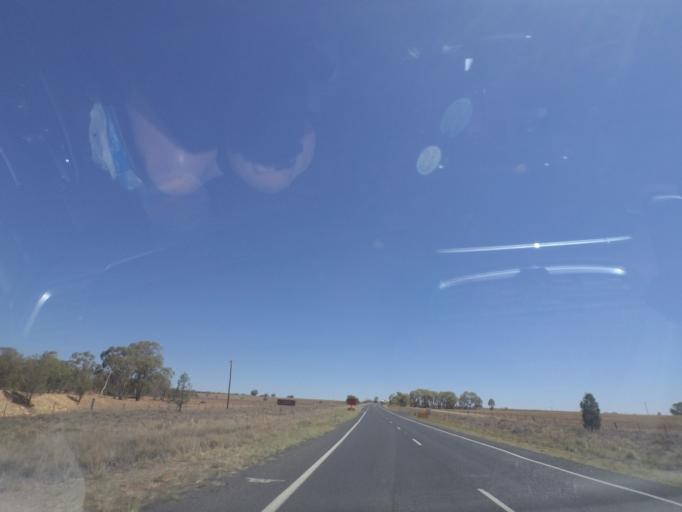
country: AU
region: New South Wales
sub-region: Gilgandra
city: Gilgandra
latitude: -31.6684
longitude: 148.7170
